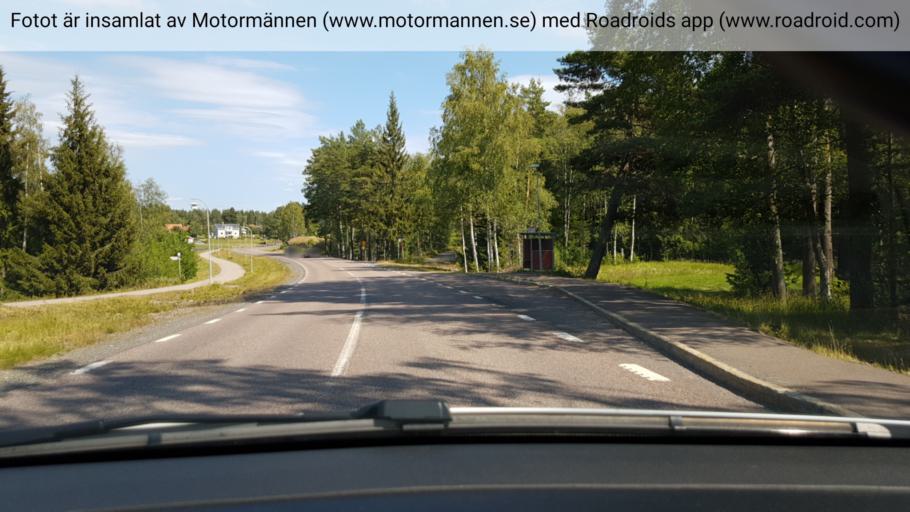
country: SE
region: Dalarna
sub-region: Faluns Kommun
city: Falun
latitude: 60.5999
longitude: 15.5682
